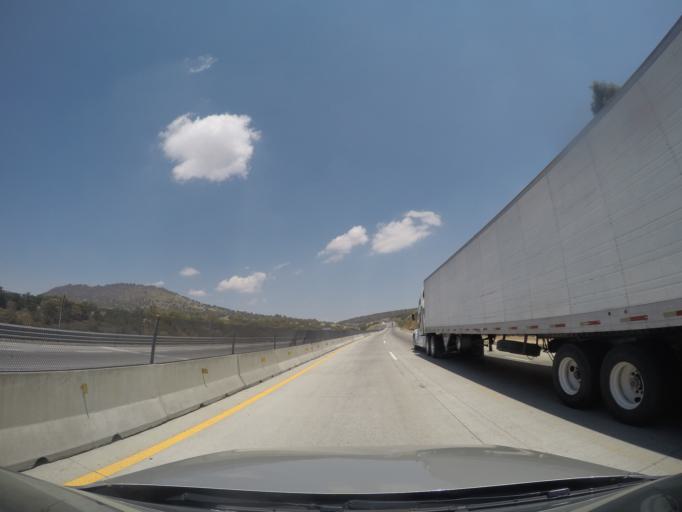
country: MX
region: Tlaxcala
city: Espanita
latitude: 19.4618
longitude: -98.4515
